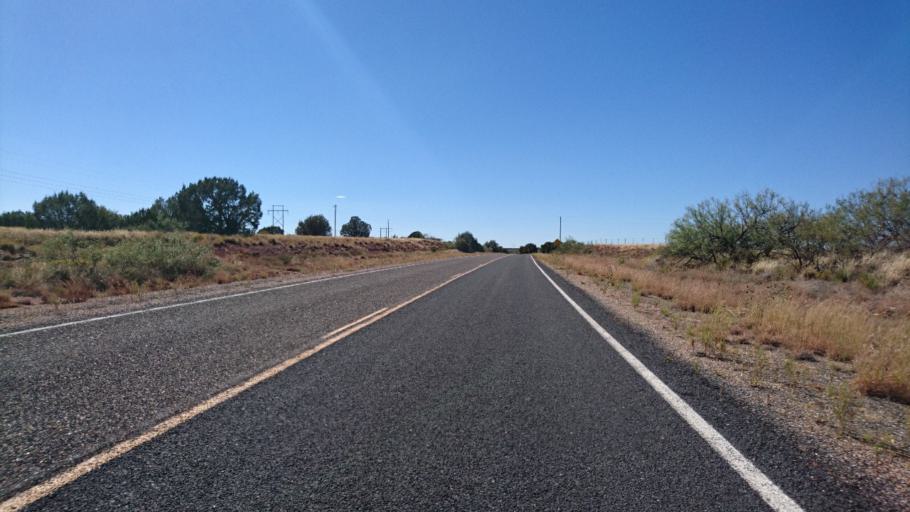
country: US
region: New Mexico
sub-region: Quay County
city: Tucumcari
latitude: 35.0680
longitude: -104.1709
